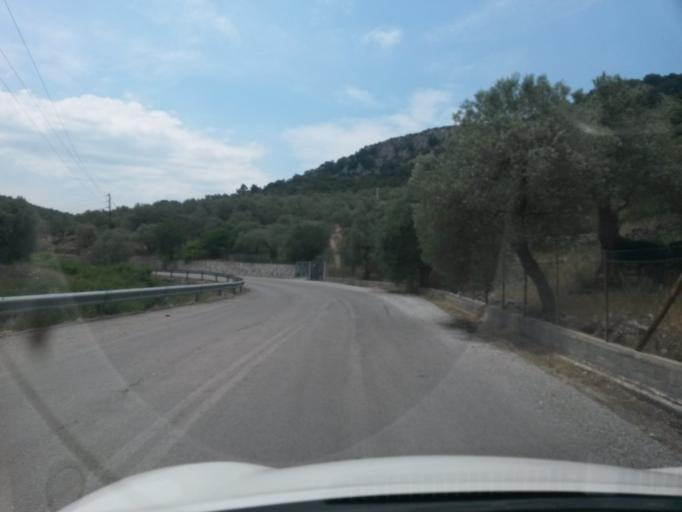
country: GR
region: North Aegean
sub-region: Nomos Lesvou
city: Pamfylla
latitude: 39.1863
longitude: 26.4365
